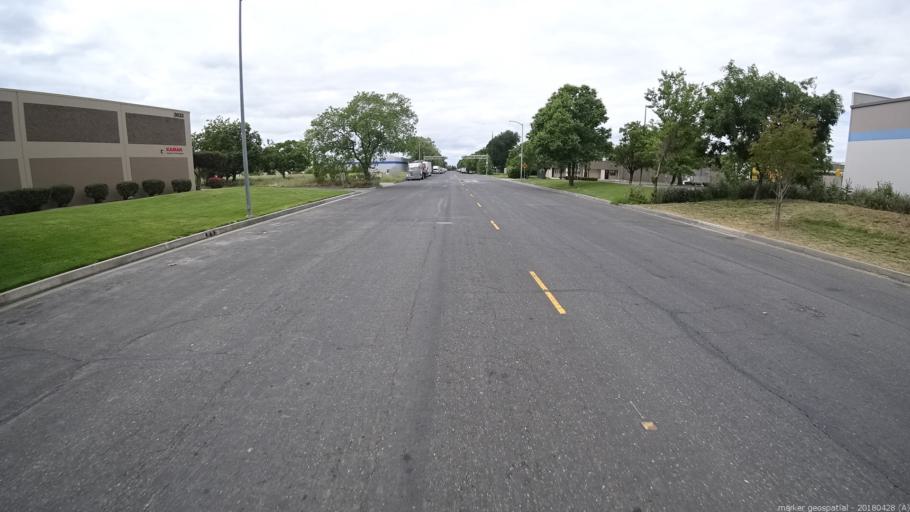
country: US
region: California
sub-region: Yolo County
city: West Sacramento
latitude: 38.5669
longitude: -121.5647
